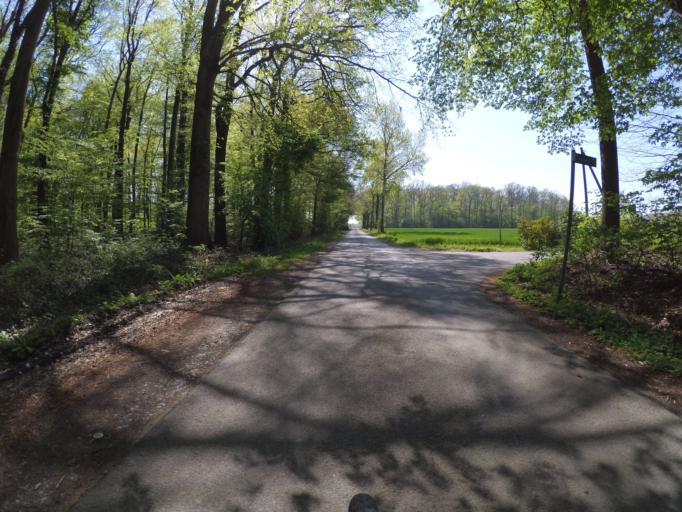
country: DE
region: North Rhine-Westphalia
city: Ludinghausen
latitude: 51.7558
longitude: 7.4412
